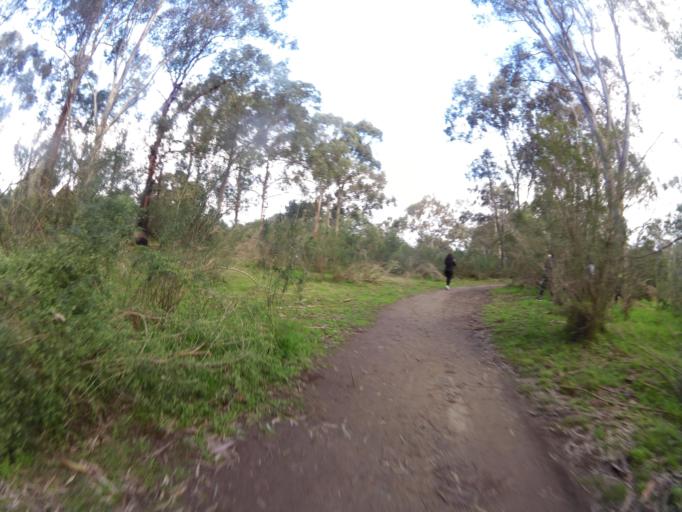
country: AU
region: Victoria
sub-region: Banyule
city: Darch
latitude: -37.7423
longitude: 145.1219
